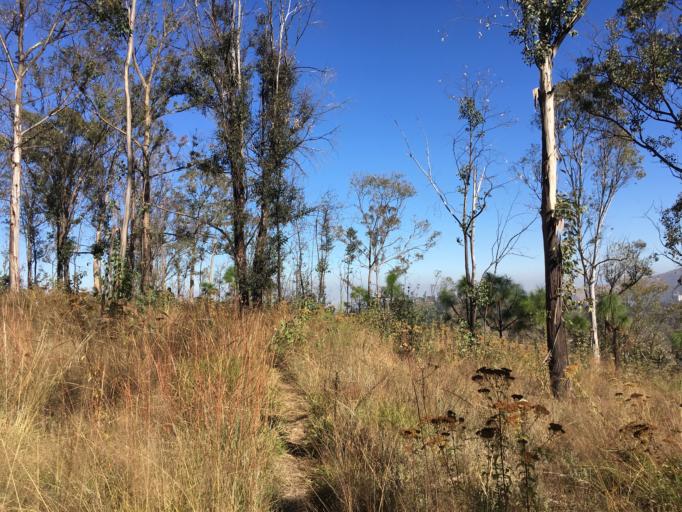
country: MX
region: Michoacan
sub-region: Morelia
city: Montana Monarca (Punta Altozano)
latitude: 19.6692
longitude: -101.1483
